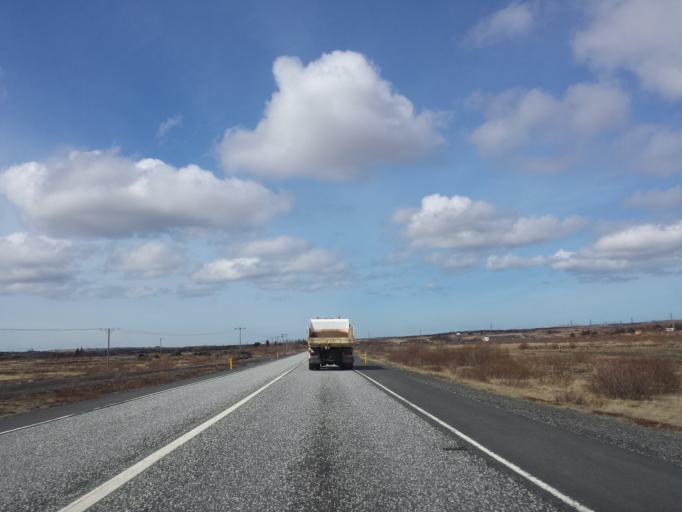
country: IS
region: Capital Region
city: Mosfellsbaer
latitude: 64.0794
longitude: -21.6625
